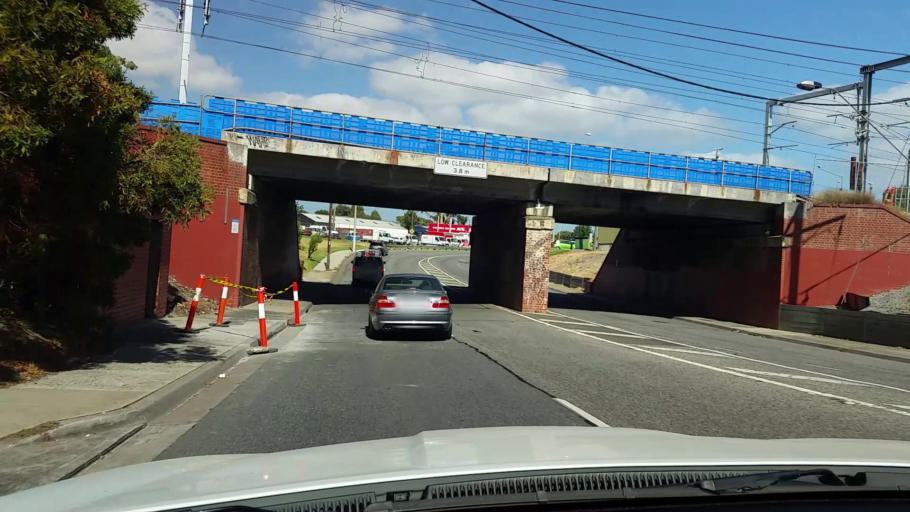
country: AU
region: Victoria
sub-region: Greater Dandenong
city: Dandenong
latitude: -37.9908
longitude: 145.2122
